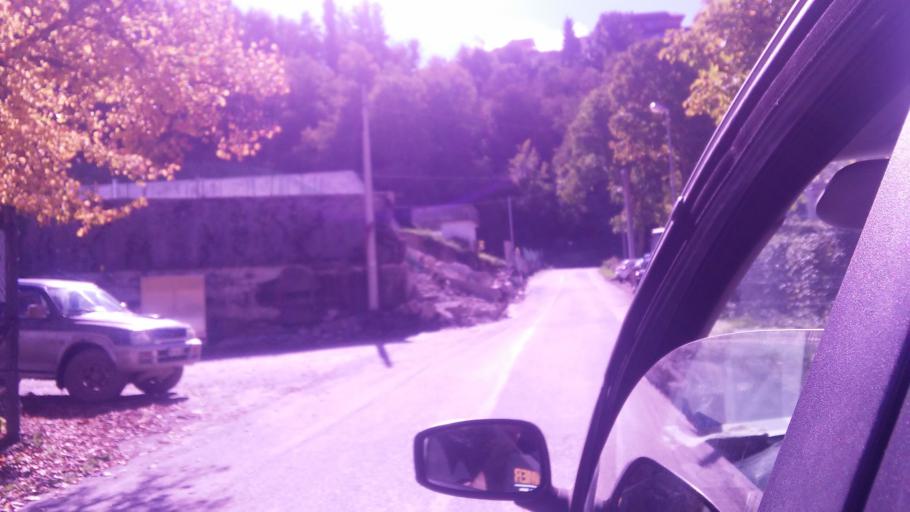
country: IT
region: Latium
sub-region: Provincia di Rieti
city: Amatrice
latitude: 42.6313
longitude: 13.2920
